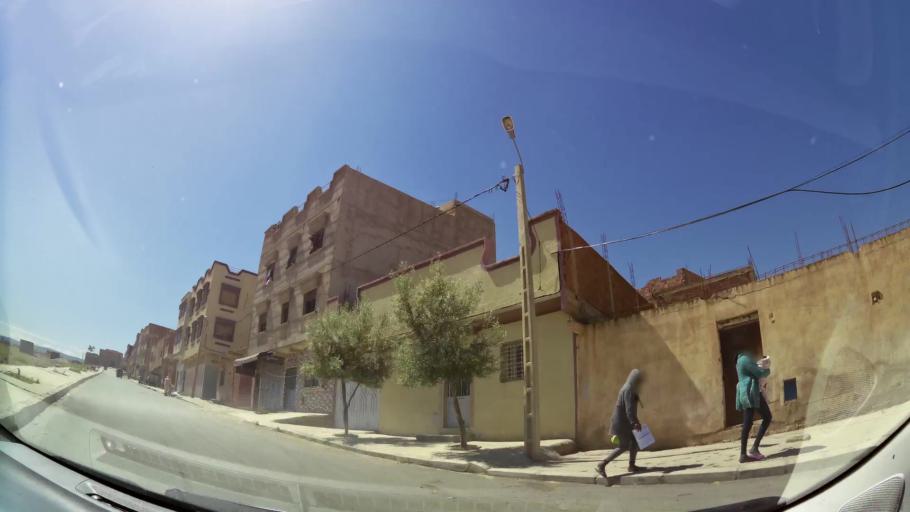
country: MA
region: Oriental
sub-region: Oujda-Angad
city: Oujda
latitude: 34.6514
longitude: -1.8751
